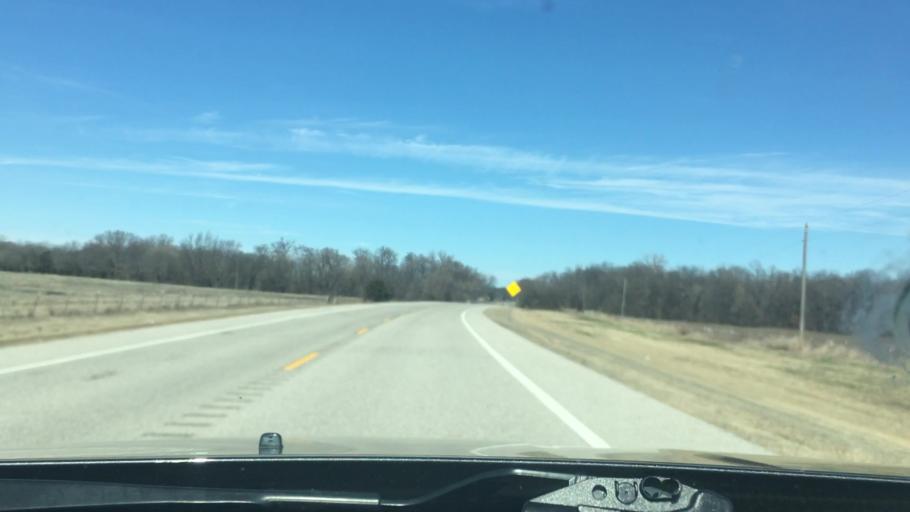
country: US
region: Oklahoma
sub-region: Murray County
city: Sulphur
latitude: 34.3872
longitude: -96.9510
